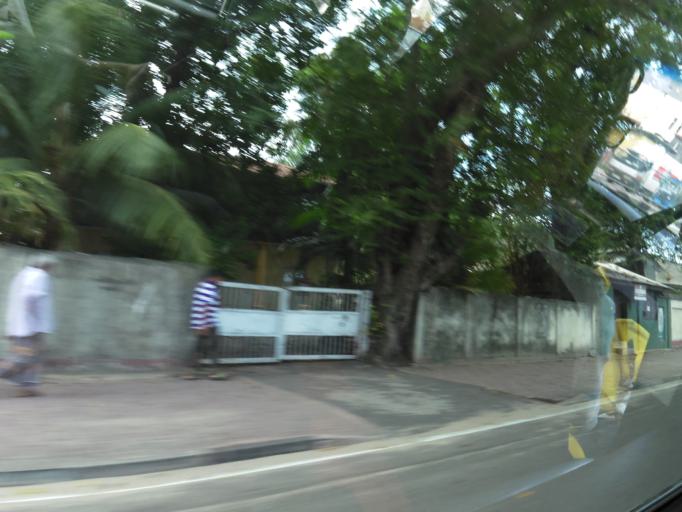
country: LK
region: Western
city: Kolonnawa
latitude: 6.9324
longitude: 79.8781
